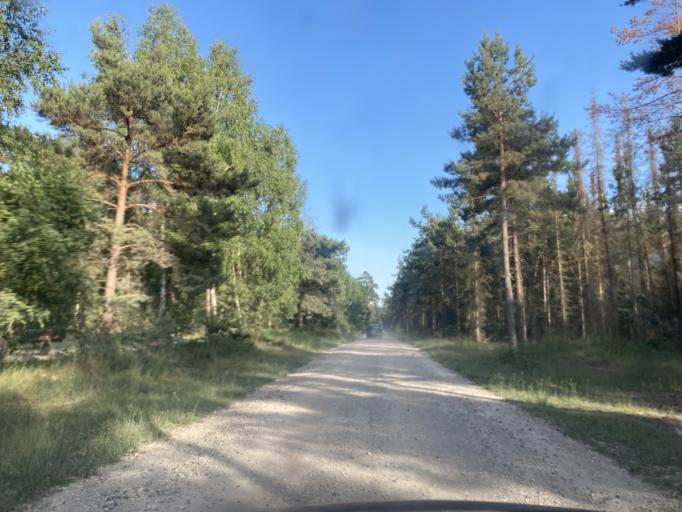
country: DK
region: Capital Region
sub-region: Halsnaes Kommune
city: Frederiksvaerk
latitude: 56.0161
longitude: 12.0132
